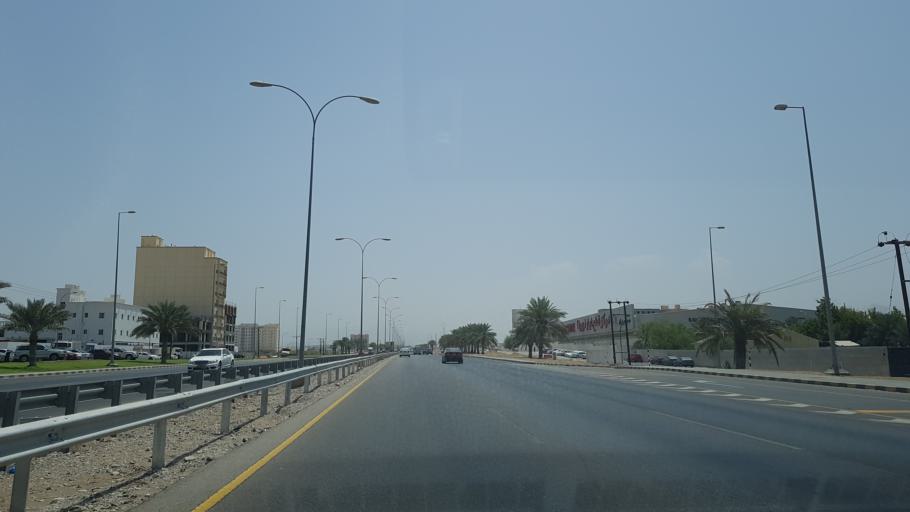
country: OM
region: Muhafazat Masqat
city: Bawshar
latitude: 23.5309
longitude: 58.5101
